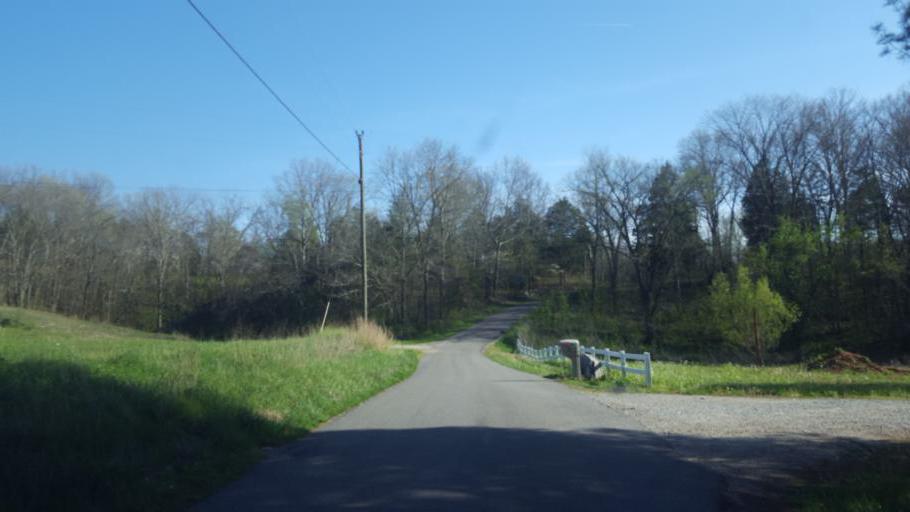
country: US
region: Kentucky
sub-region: Barren County
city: Cave City
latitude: 37.1958
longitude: -86.0117
